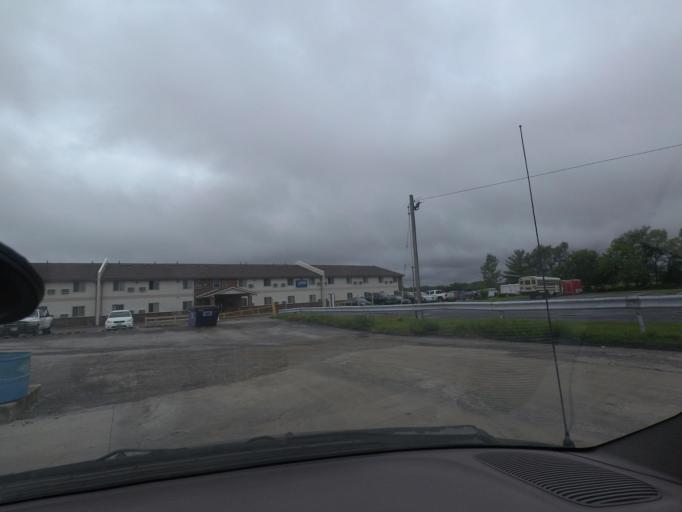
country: US
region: Illinois
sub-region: Macon County
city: Harristown
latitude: 39.8462
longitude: -89.0295
